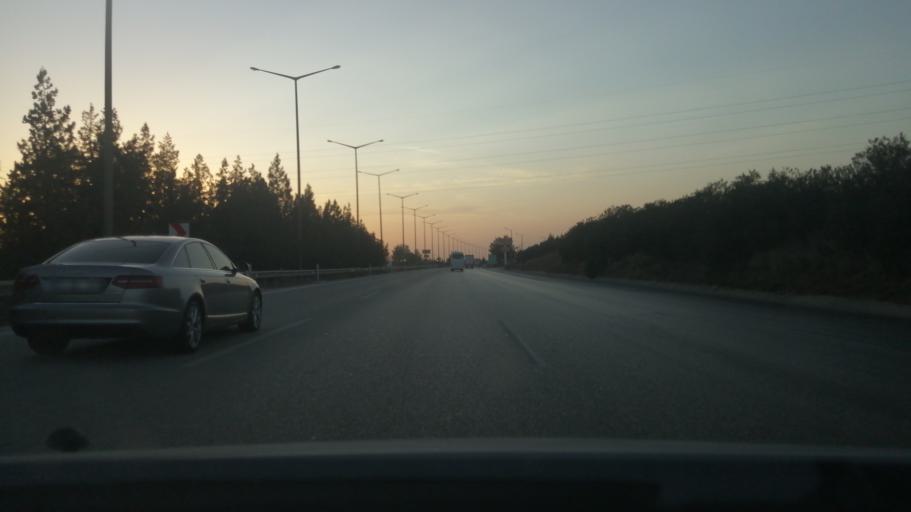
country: TR
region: Adana
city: Yuregir
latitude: 37.0216
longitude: 35.4804
